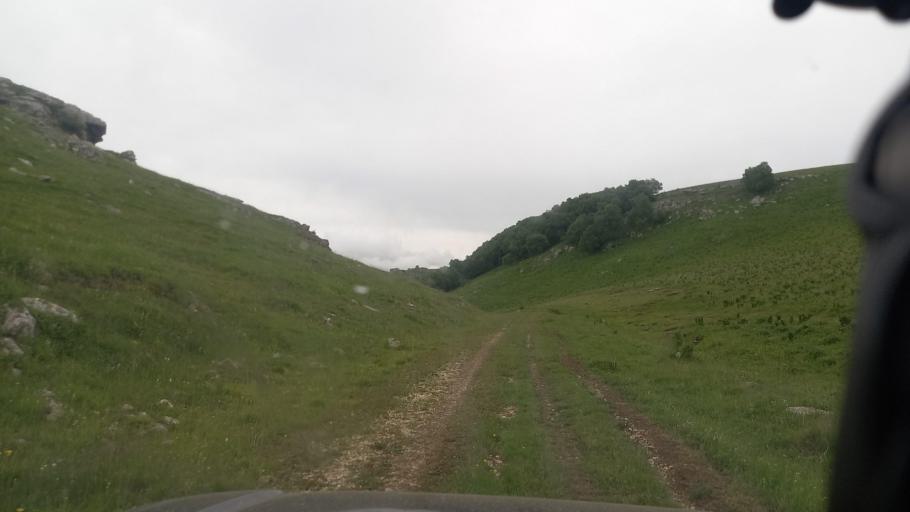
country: RU
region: Karachayevo-Cherkesiya
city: Pregradnaya
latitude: 43.9853
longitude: 41.3037
